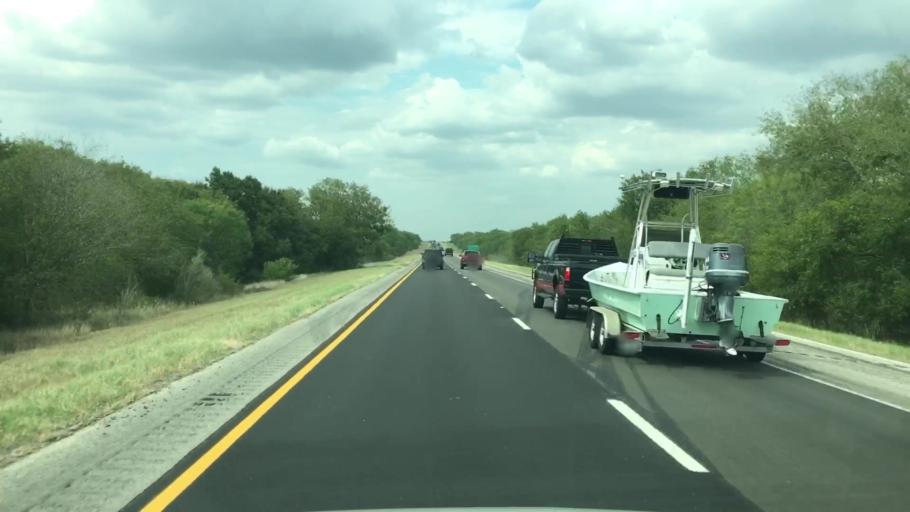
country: US
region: Texas
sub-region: Atascosa County
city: Pleasanton
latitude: 28.9302
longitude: -98.4352
